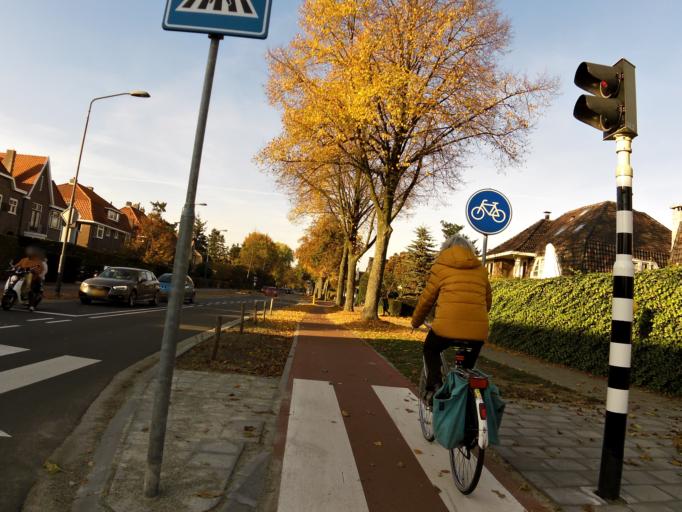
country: NL
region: North Brabant
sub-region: Gemeente Vught
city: Vught
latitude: 51.6681
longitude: 5.2937
